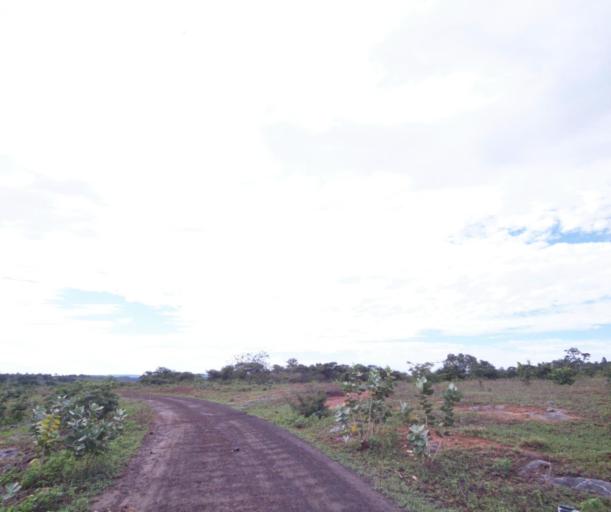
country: BR
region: Bahia
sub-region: Carinhanha
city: Carinhanha
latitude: -14.2245
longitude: -44.4393
